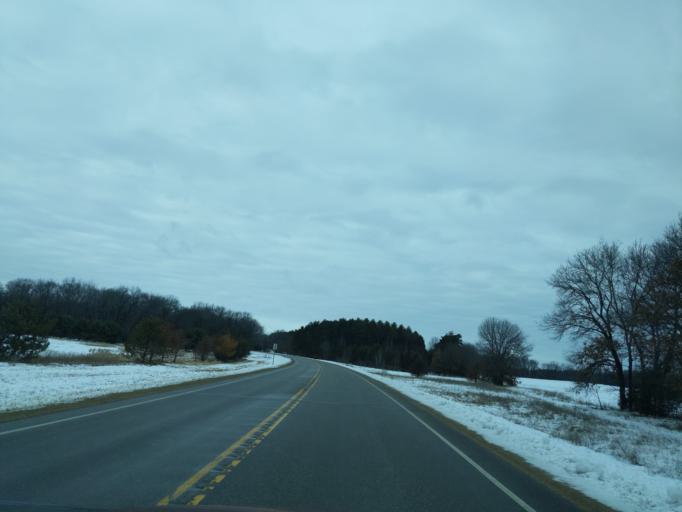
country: US
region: Wisconsin
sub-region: Waushara County
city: Wautoma
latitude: 43.9361
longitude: -89.3124
